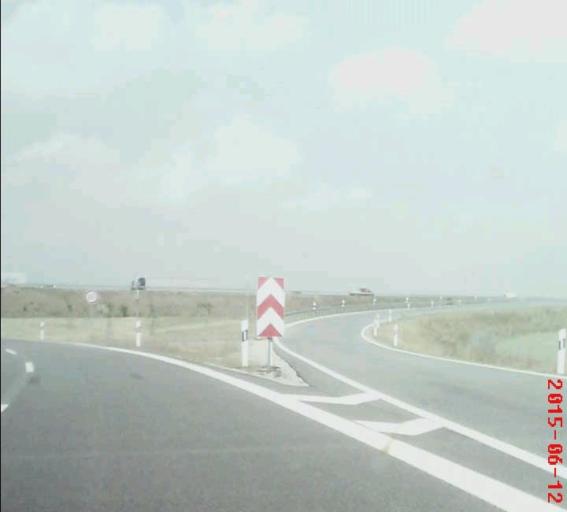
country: DE
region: Saxony-Anhalt
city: Oberroblingen
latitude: 51.4385
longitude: 11.3320
